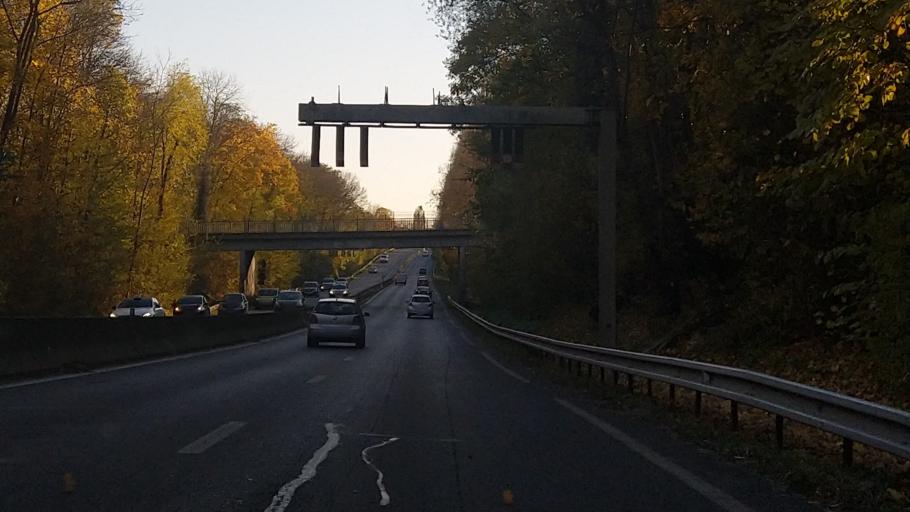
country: FR
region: Ile-de-France
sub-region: Departement du Val-d'Oise
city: Saint-Brice-sous-Foret
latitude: 49.0013
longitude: 2.3594
